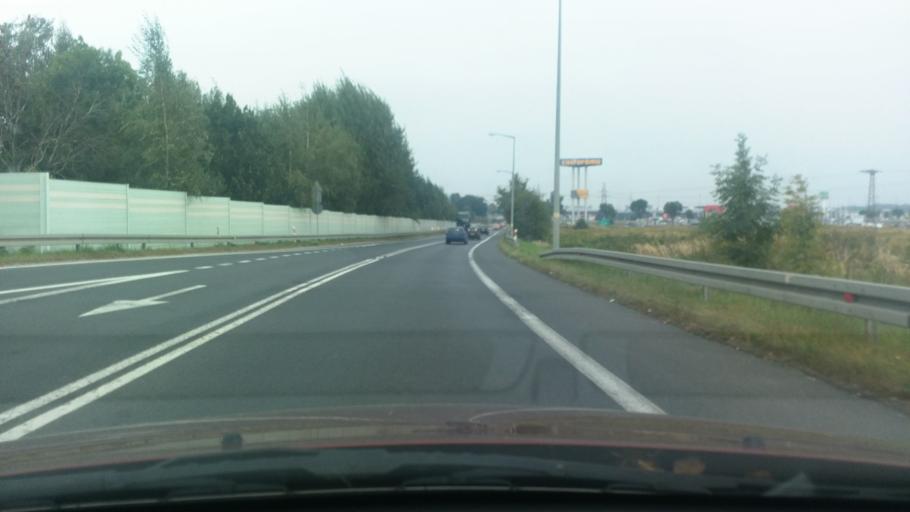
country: PL
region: Lower Silesian Voivodeship
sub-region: Powiat zgorzelecki
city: Lagow
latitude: 51.1507
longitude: 15.0288
